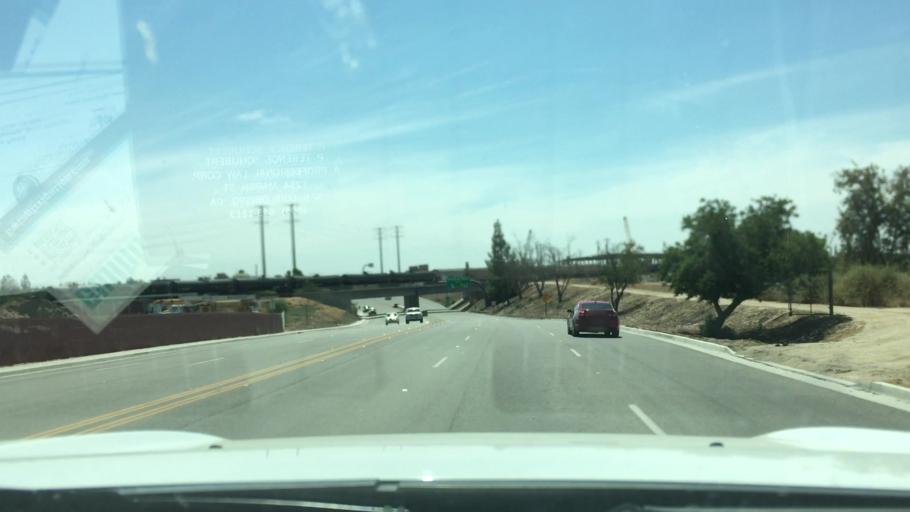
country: US
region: California
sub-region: Kern County
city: Bakersfield
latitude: 35.3727
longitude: -119.0528
